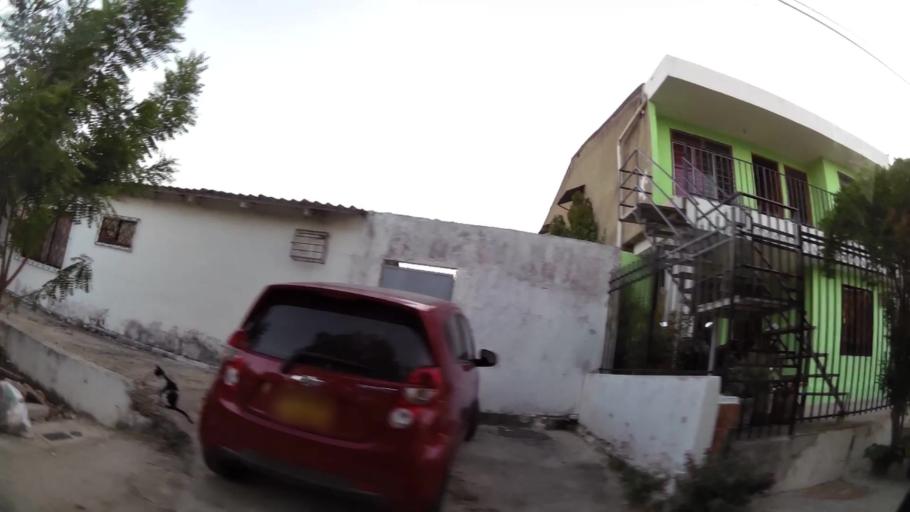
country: CO
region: Bolivar
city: Cartagena
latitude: 10.3869
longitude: -75.4889
